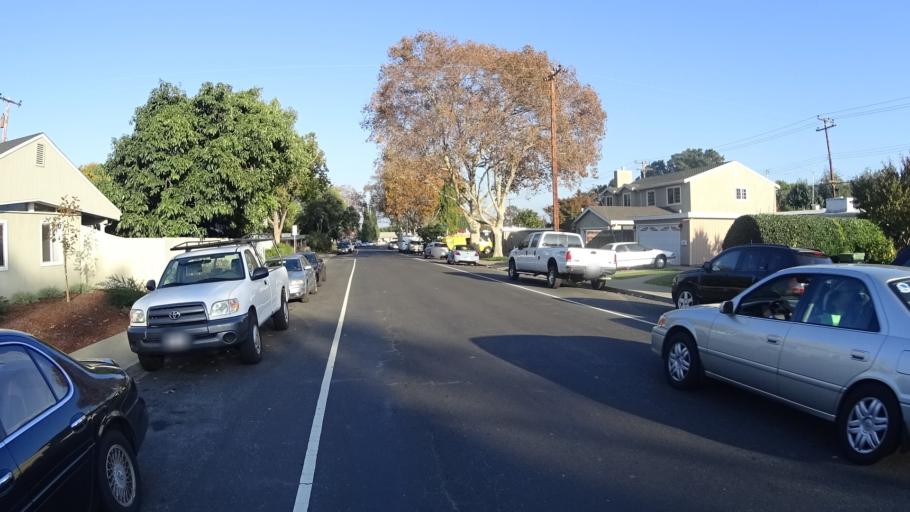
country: US
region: California
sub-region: Santa Clara County
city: Santa Clara
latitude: 37.3500
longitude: -121.9891
